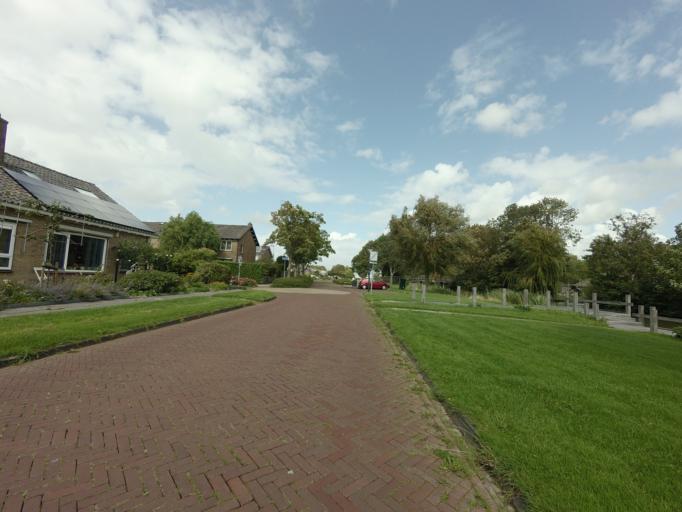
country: NL
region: Friesland
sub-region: Gemeente Franekeradeel
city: Franeker
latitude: 53.1899
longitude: 5.5462
